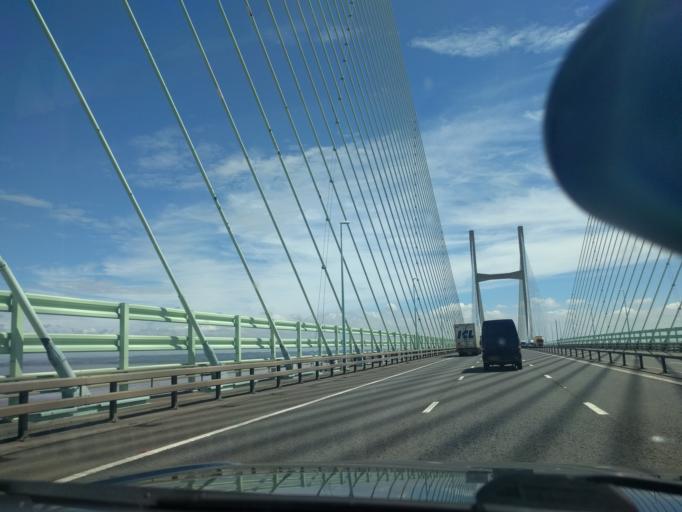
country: GB
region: England
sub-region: South Gloucestershire
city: Severn Beach
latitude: 51.5750
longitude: -2.7029
